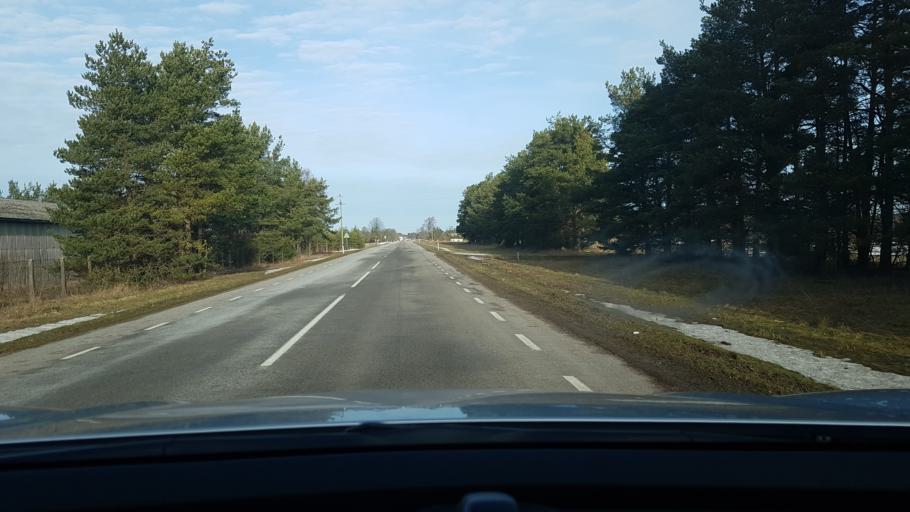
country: EE
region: Saare
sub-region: Kuressaare linn
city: Kuressaare
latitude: 58.5145
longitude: 22.7046
